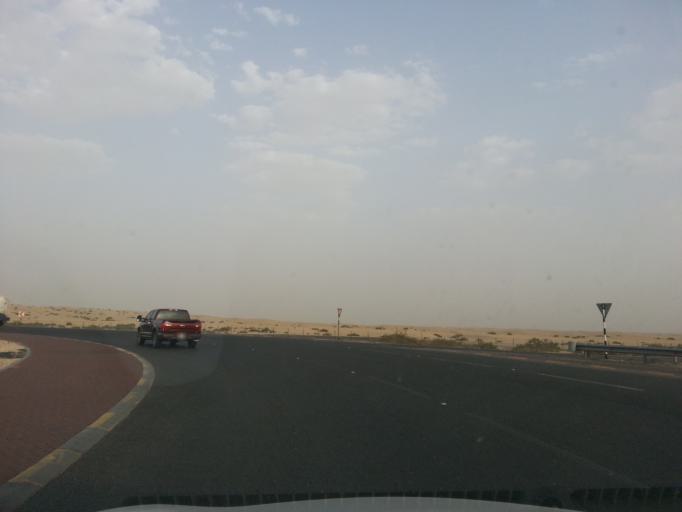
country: AE
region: Dubai
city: Dubai
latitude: 24.5948
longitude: 55.1217
